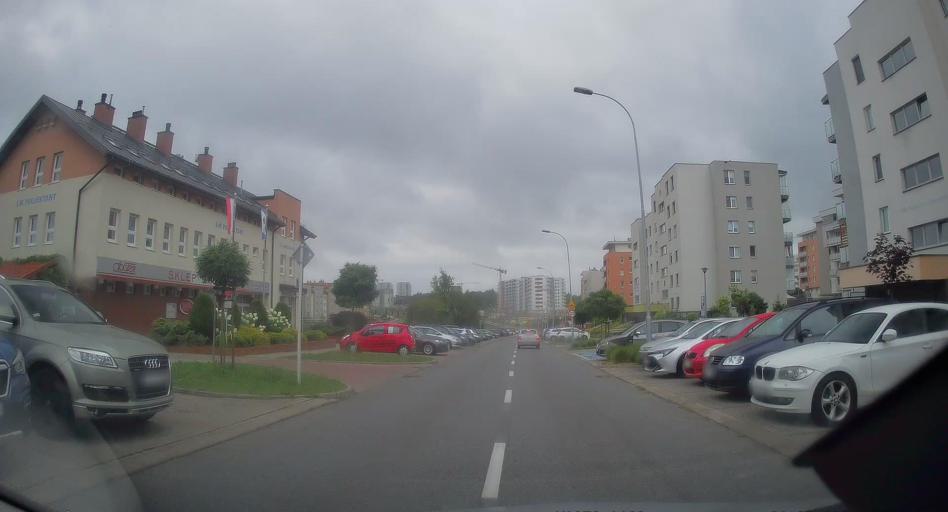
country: PL
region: Subcarpathian Voivodeship
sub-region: Rzeszow
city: Przybyszowka
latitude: 50.0474
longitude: 21.9516
